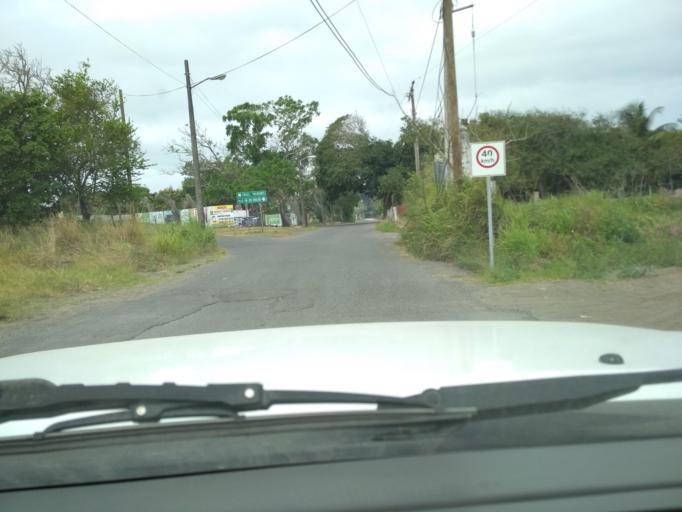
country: MX
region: Veracruz
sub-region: Medellin
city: Fraccionamiento Arboledas San Ramon
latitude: 19.0896
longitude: -96.1353
